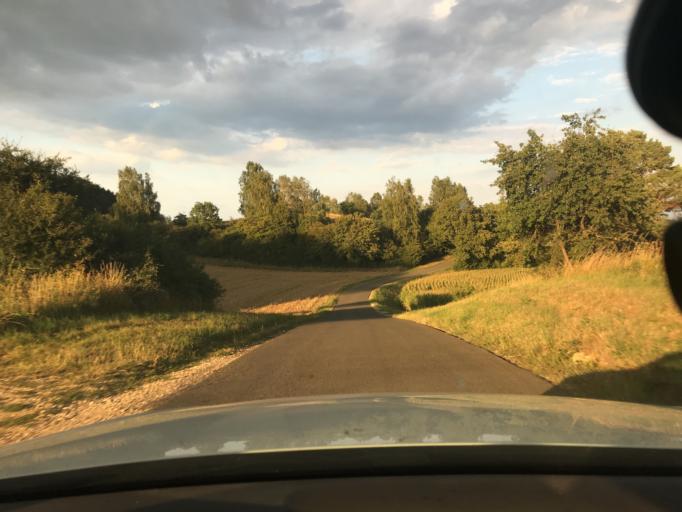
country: DE
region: Bavaria
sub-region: Upper Franconia
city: Pegnitz
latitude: 49.7465
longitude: 11.5783
